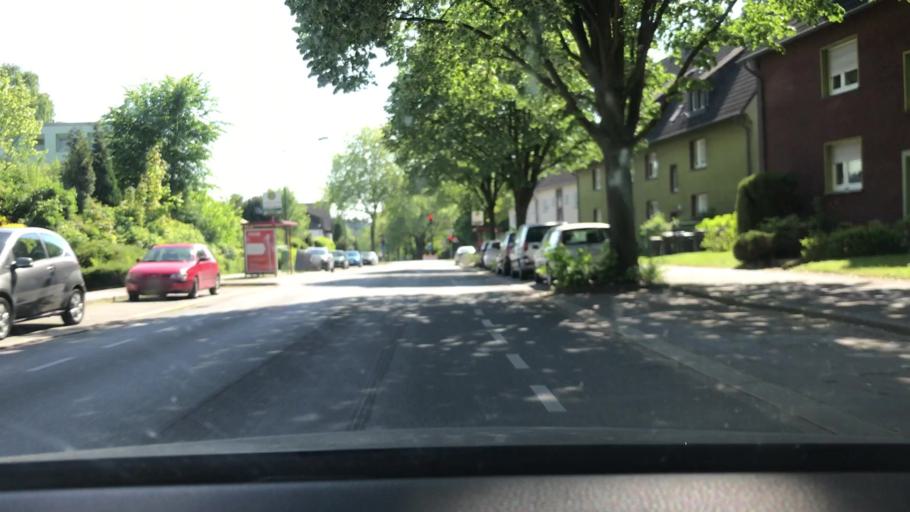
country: DE
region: North Rhine-Westphalia
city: Herten
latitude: 51.6045
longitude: 7.1431
